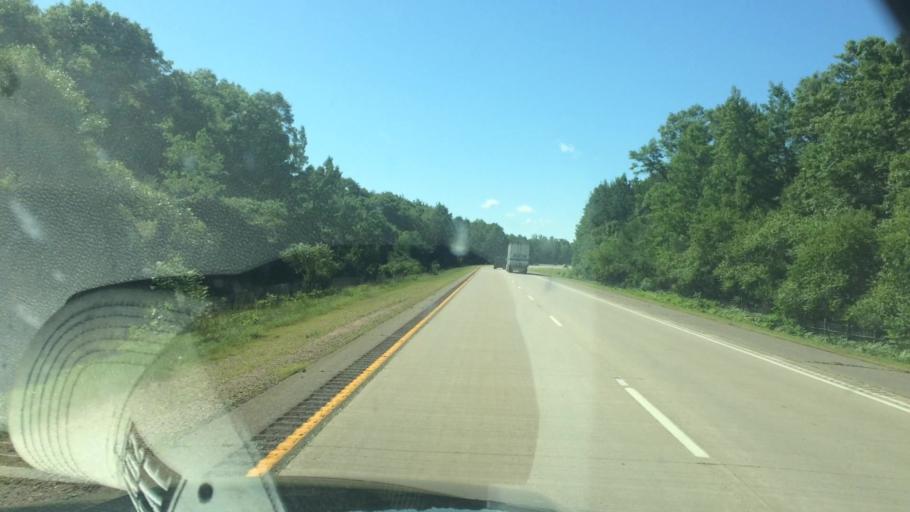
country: US
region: Wisconsin
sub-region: Marathon County
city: Mosinee
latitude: 44.6927
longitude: -89.6442
